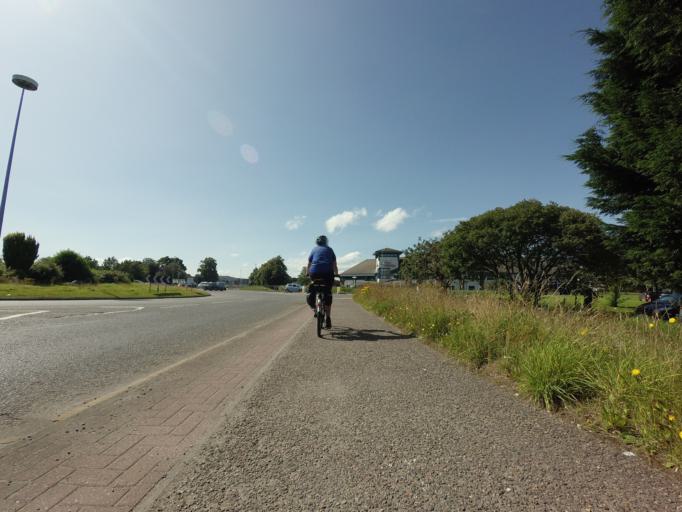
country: GB
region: Scotland
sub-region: Highland
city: Inverness
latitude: 57.4719
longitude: -4.1894
